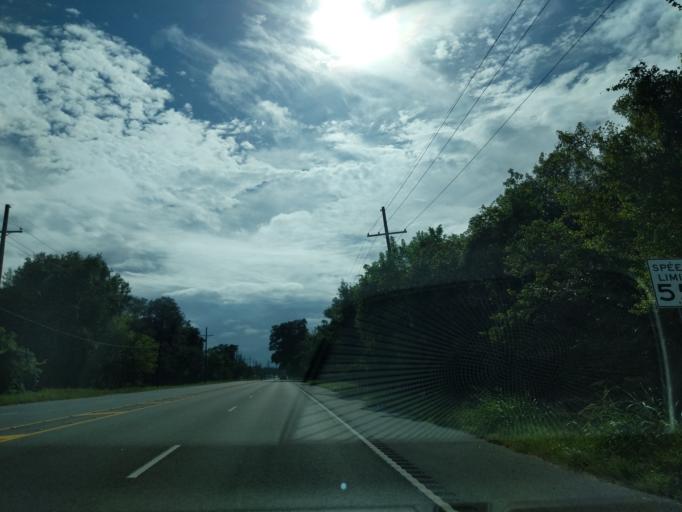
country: US
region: Louisiana
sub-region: Saint Bernard Parish
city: Chalmette
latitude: 30.0458
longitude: -89.8908
